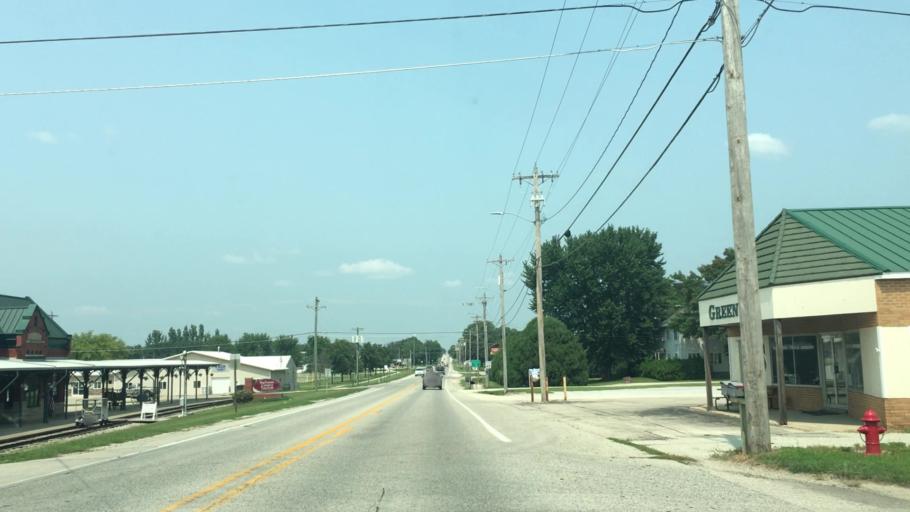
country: US
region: Iowa
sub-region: Buchanan County
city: Independence
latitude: 42.4782
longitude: -91.8894
